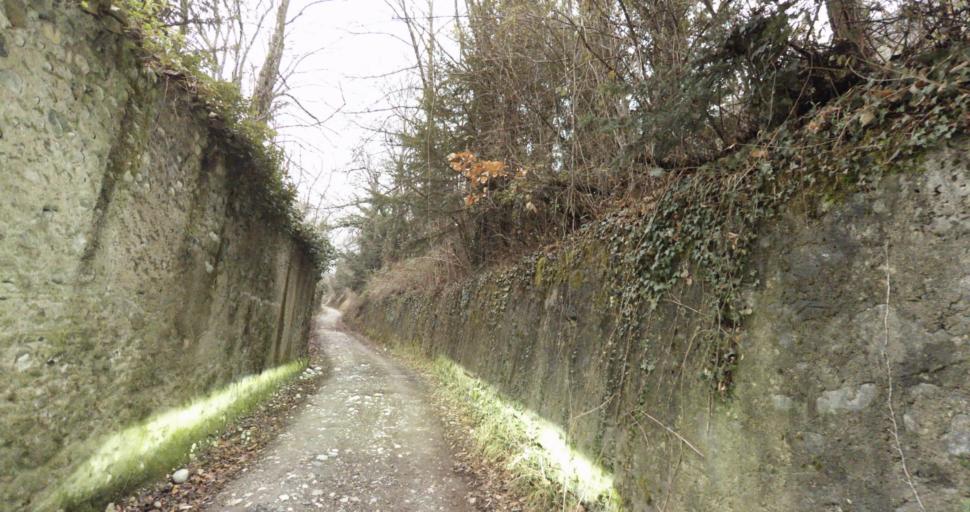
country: FR
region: Rhone-Alpes
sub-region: Departement de l'Isere
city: Vif
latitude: 45.0563
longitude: 5.6642
